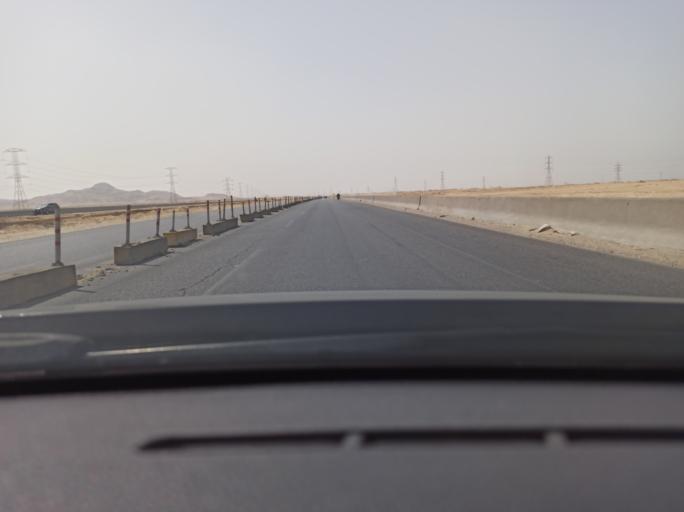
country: EG
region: Muhafazat Bani Suwayf
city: Bush
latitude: 29.1422
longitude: 31.2291
